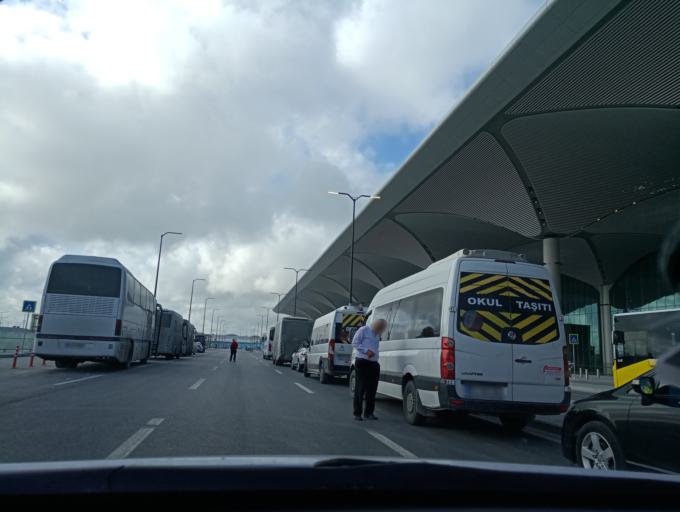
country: TR
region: Istanbul
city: Durusu
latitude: 41.2587
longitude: 28.7433
